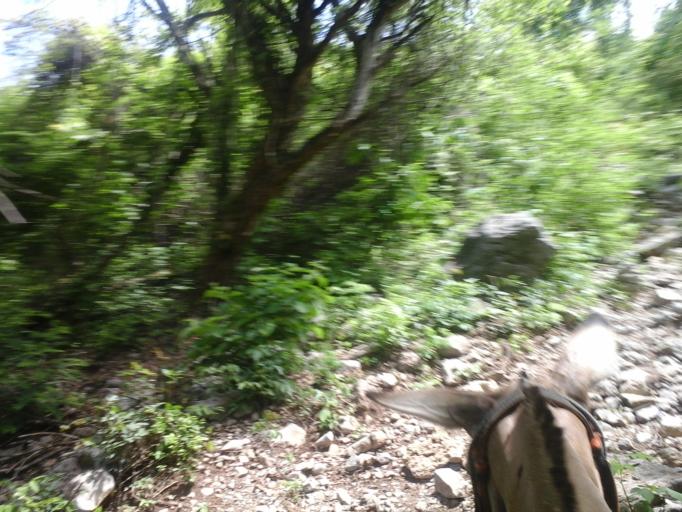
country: CO
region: Cesar
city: Becerril
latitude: 9.7456
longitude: -73.1673
